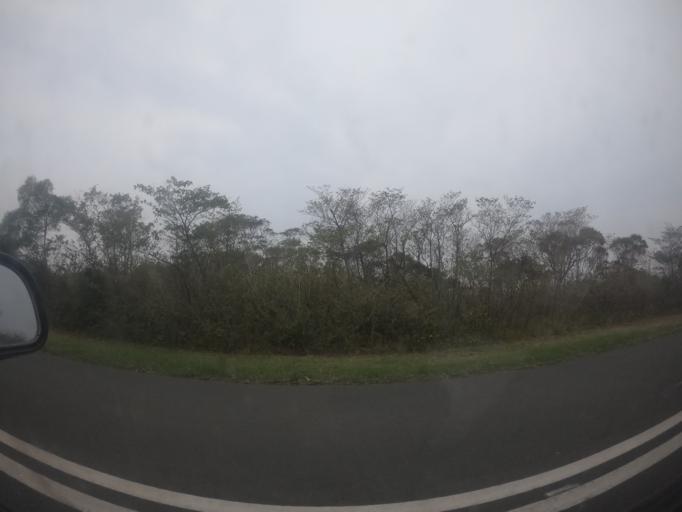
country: AU
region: New South Wales
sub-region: Shellharbour
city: Croom
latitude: -34.6125
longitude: 150.8550
